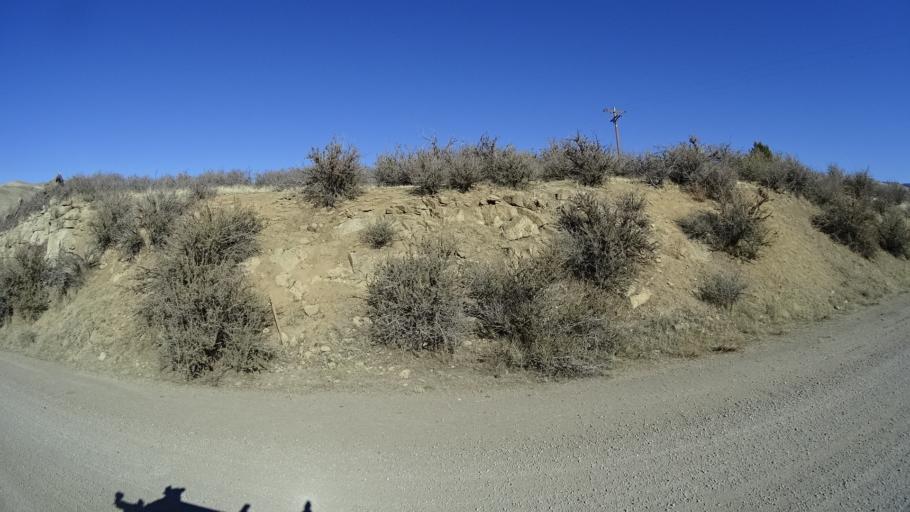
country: US
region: California
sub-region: Siskiyou County
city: Montague
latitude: 41.8320
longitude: -122.3737
